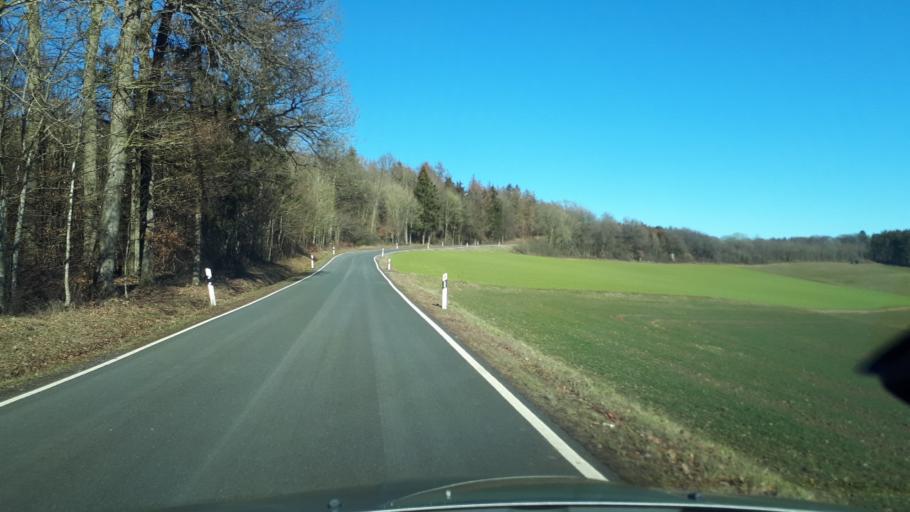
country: DE
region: Rheinland-Pfalz
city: Ellscheid
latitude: 50.1653
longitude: 6.9141
